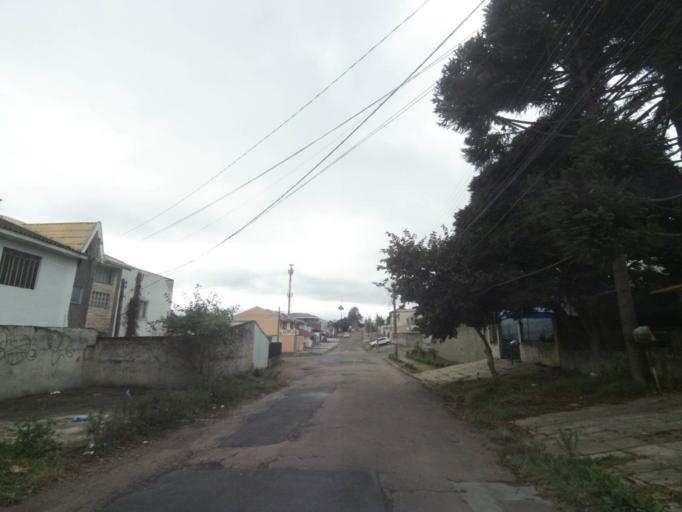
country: BR
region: Parana
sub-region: Curitiba
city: Curitiba
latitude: -25.5000
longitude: -49.2882
